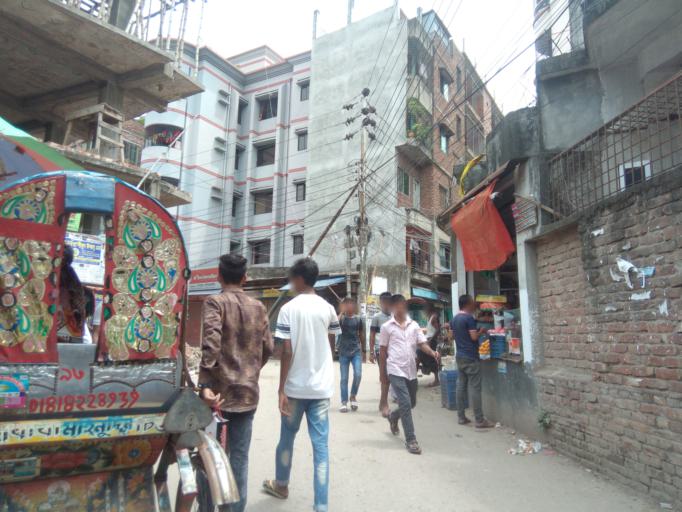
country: BD
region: Dhaka
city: Azimpur
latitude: 23.7267
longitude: 90.3727
